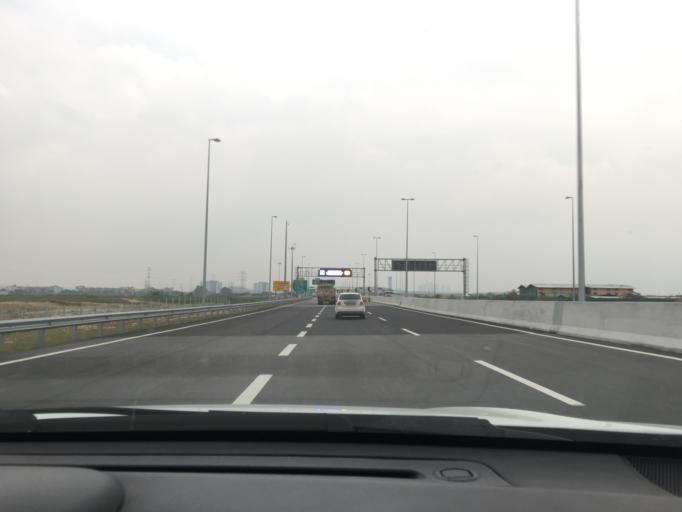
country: MY
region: Selangor
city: Klang
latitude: 3.0961
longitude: 101.4329
